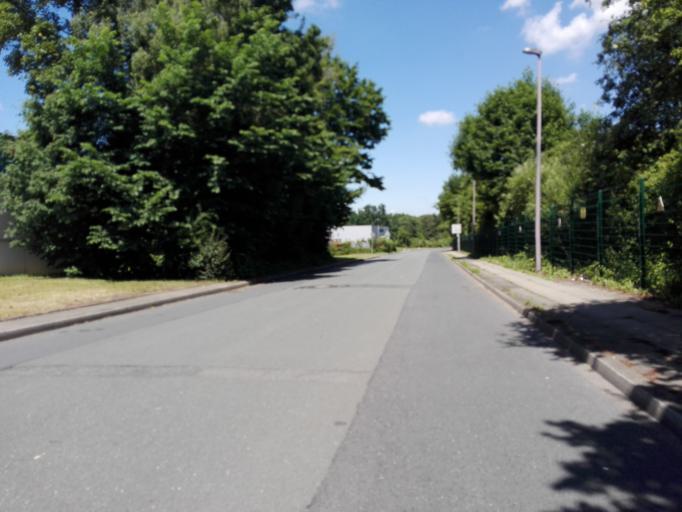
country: DE
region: North Rhine-Westphalia
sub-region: Regierungsbezirk Arnsberg
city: Unna
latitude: 51.5331
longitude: 7.7170
